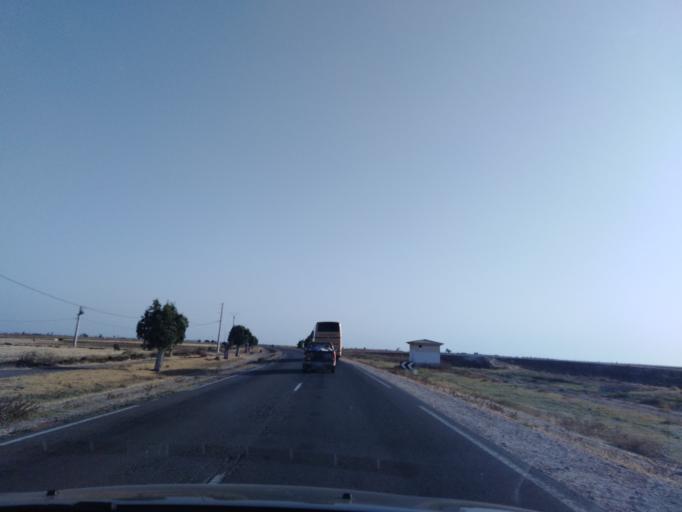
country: MA
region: Doukkala-Abda
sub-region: Safi
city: Youssoufia
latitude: 32.4884
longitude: -8.7653
